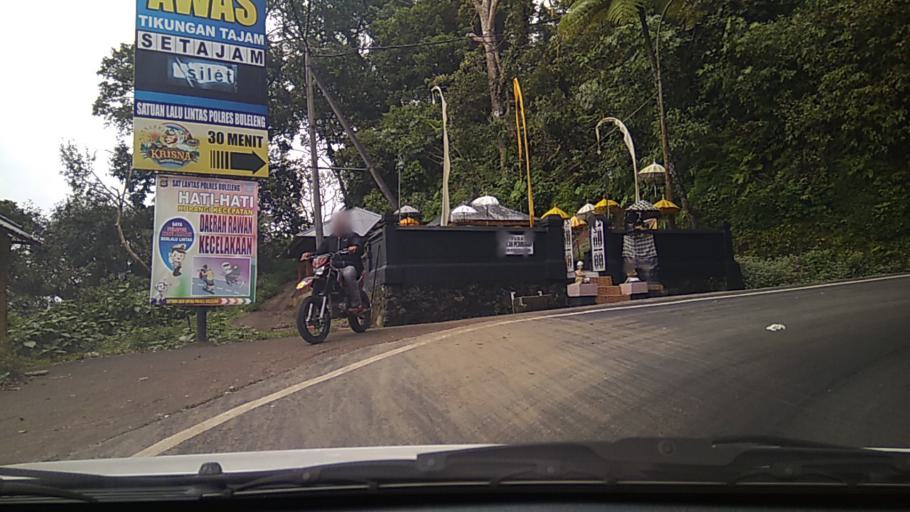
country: ID
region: Bali
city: Munduk
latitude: -8.2375
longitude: 115.1381
